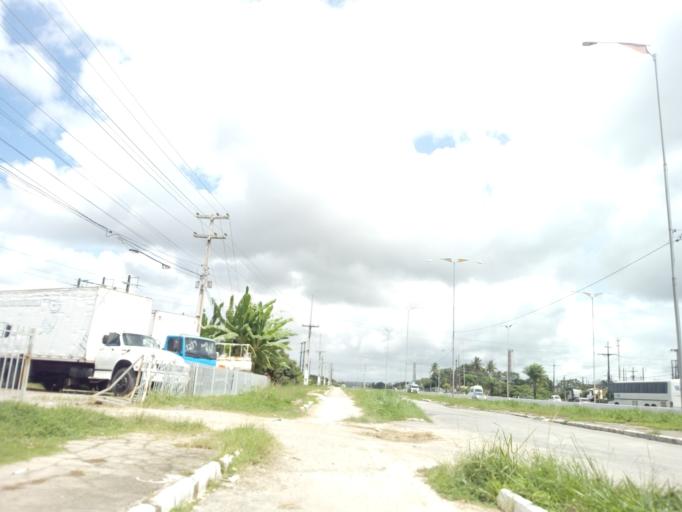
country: BR
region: Pernambuco
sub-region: Cabo De Santo Agostinho
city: Cabo
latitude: -8.2714
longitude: -35.0234
